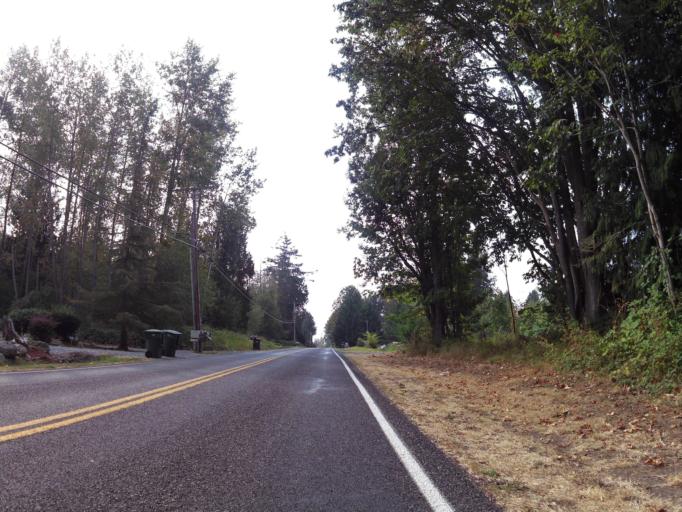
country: US
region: Washington
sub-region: Whatcom County
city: Ferndale
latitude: 48.8100
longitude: -122.6828
